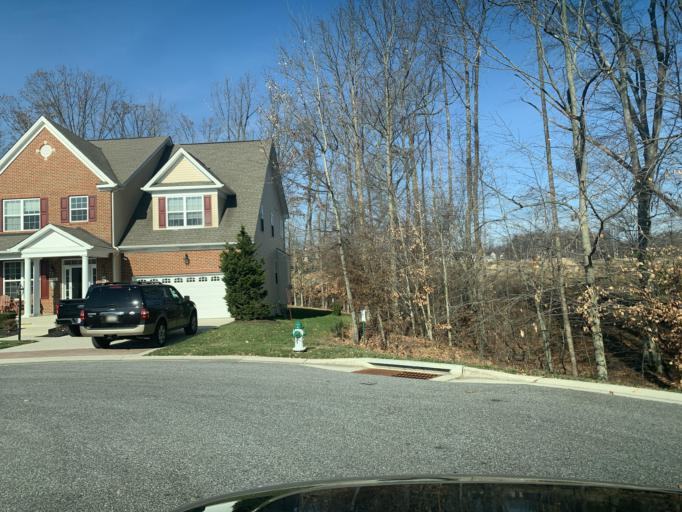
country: US
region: Maryland
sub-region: Harford County
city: Havre de Grace
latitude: 39.5441
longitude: -76.1182
